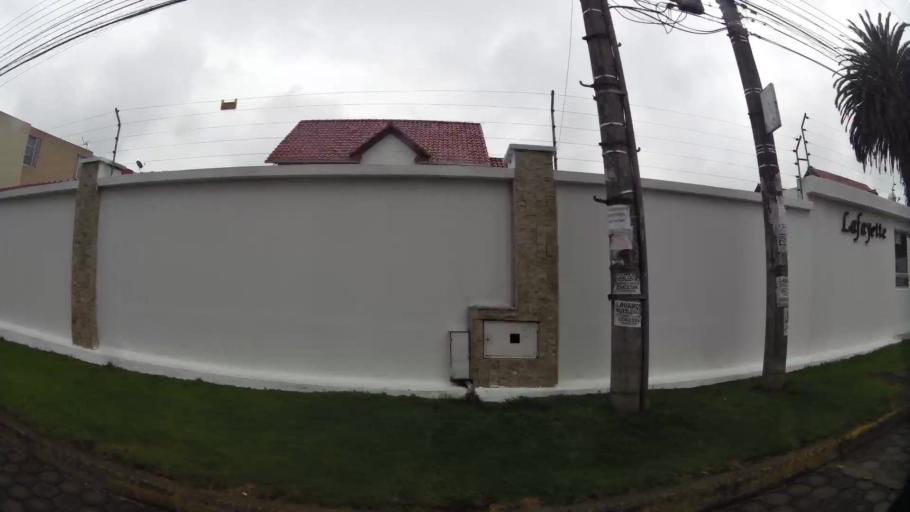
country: EC
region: Pichincha
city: Sangolqui
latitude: -0.2790
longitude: -78.4652
